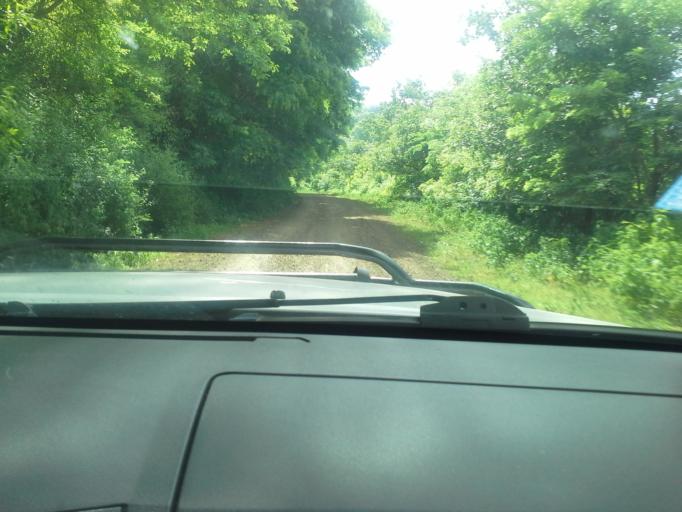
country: NI
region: Matagalpa
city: Terrabona
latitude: 12.7002
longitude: -85.9436
